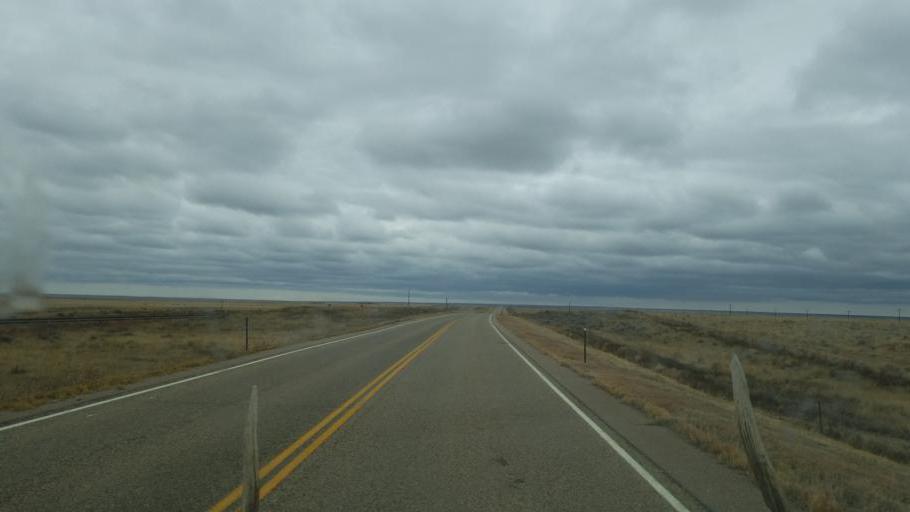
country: US
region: Colorado
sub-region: Kiowa County
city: Eads
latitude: 38.7732
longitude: -102.7528
